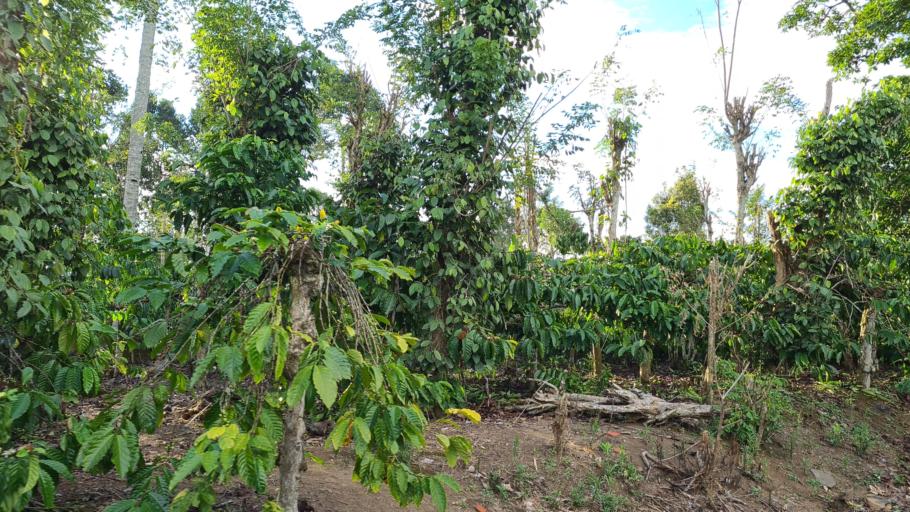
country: ID
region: Lampung
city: Kenali
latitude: -5.0603
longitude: 104.4106
